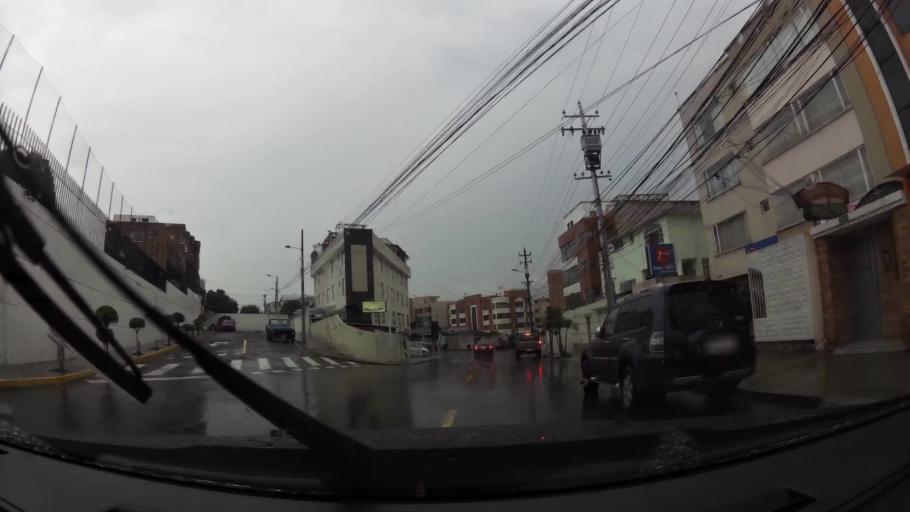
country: EC
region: Pichincha
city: Quito
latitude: -0.1594
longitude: -78.4616
